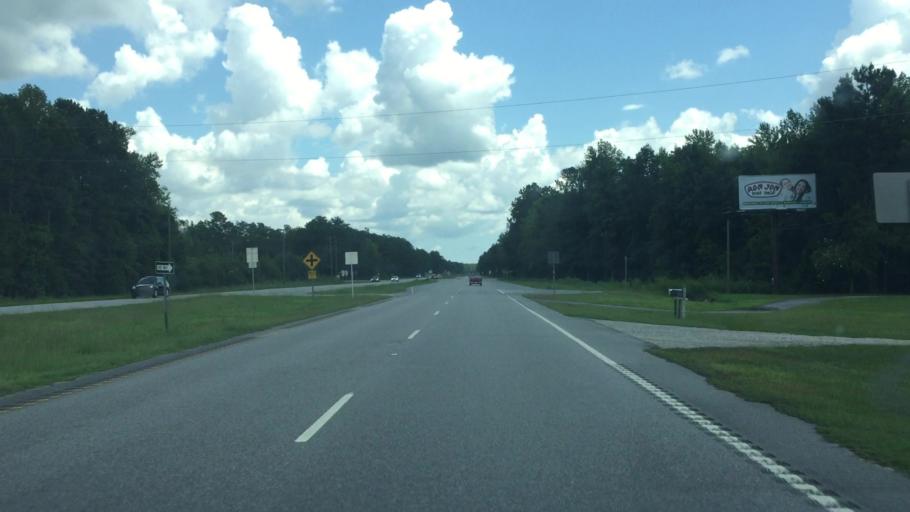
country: US
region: South Carolina
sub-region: Horry County
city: Loris
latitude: 34.0412
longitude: -78.8223
